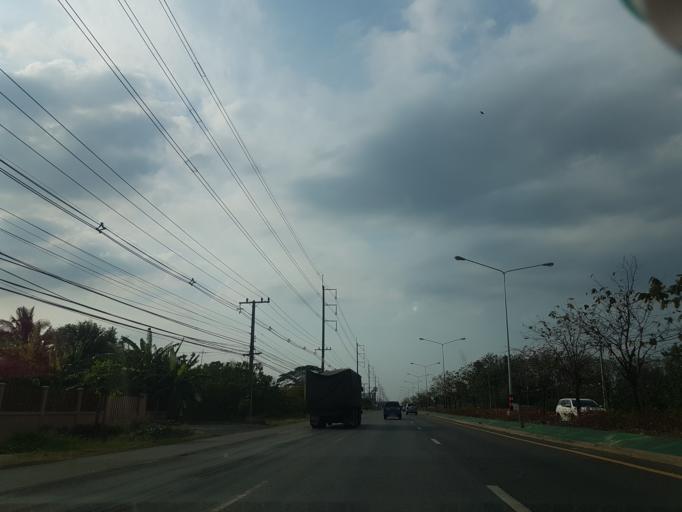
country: TH
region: Sara Buri
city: Phra Phutthabat
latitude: 14.7408
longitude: 100.7648
